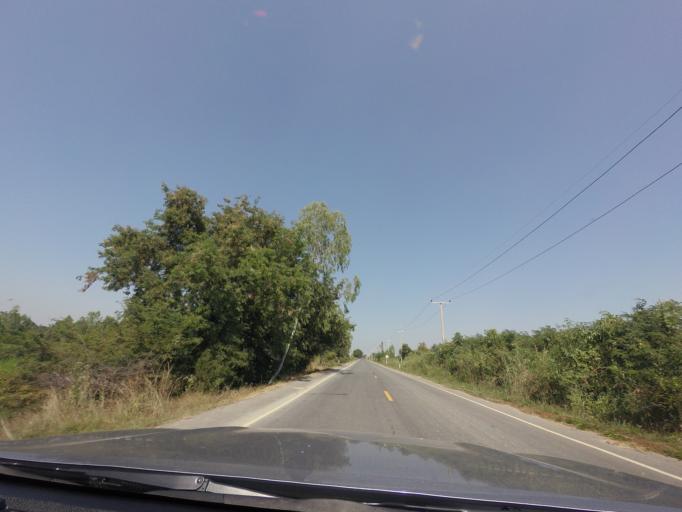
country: TH
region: Sukhothai
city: Sukhothai
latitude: 17.0779
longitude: 99.7907
